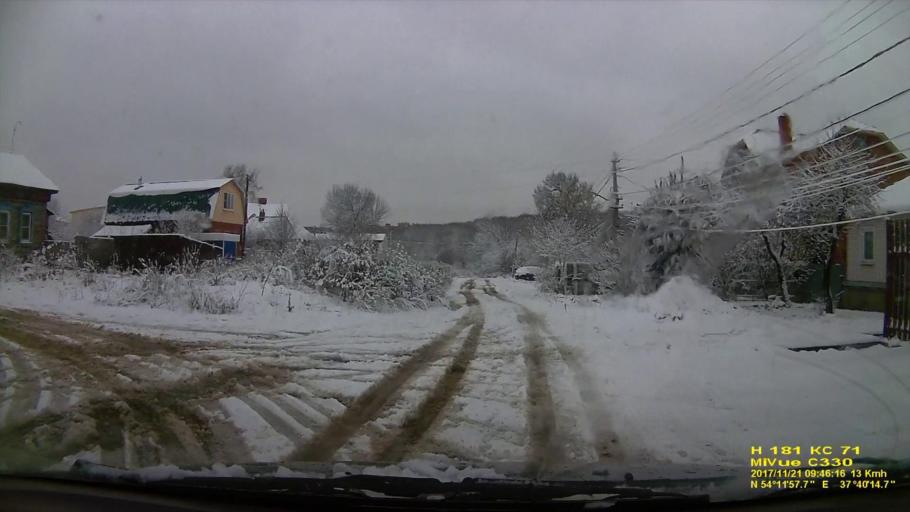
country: RU
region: Tula
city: Tula
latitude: 54.1994
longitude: 37.6706
